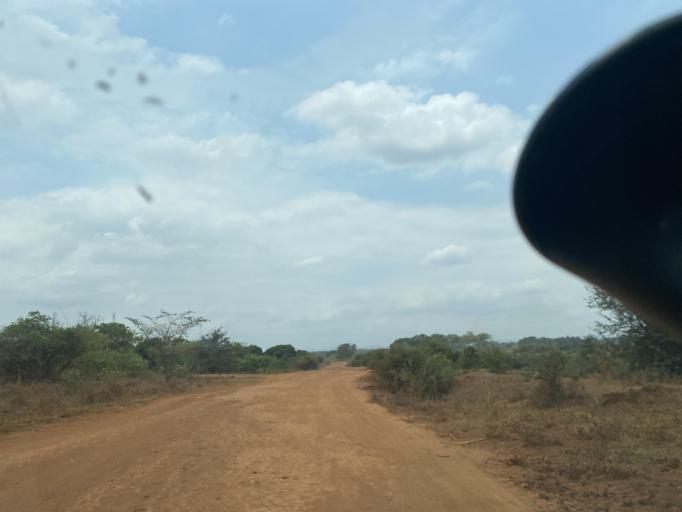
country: ZM
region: Lusaka
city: Chongwe
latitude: -15.5046
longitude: 28.8134
